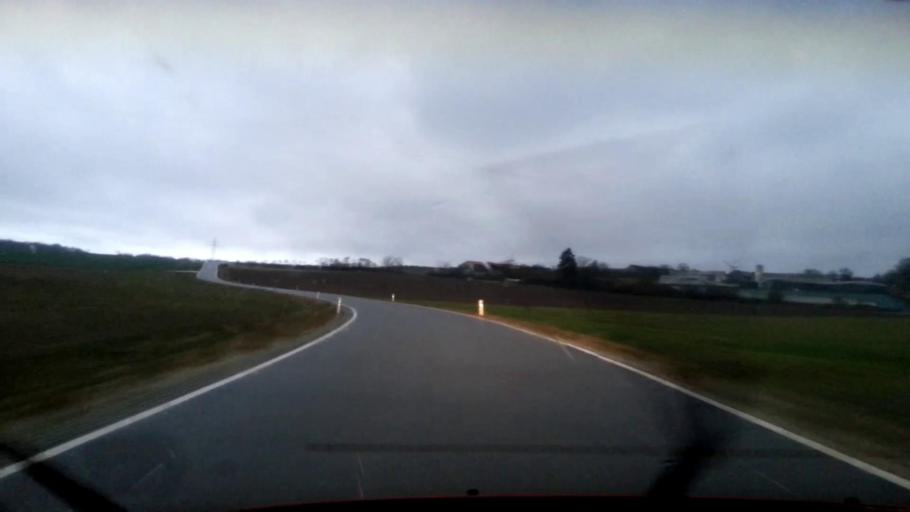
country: DE
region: Bavaria
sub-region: Upper Franconia
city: Poxdorf
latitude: 49.9667
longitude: 11.1345
